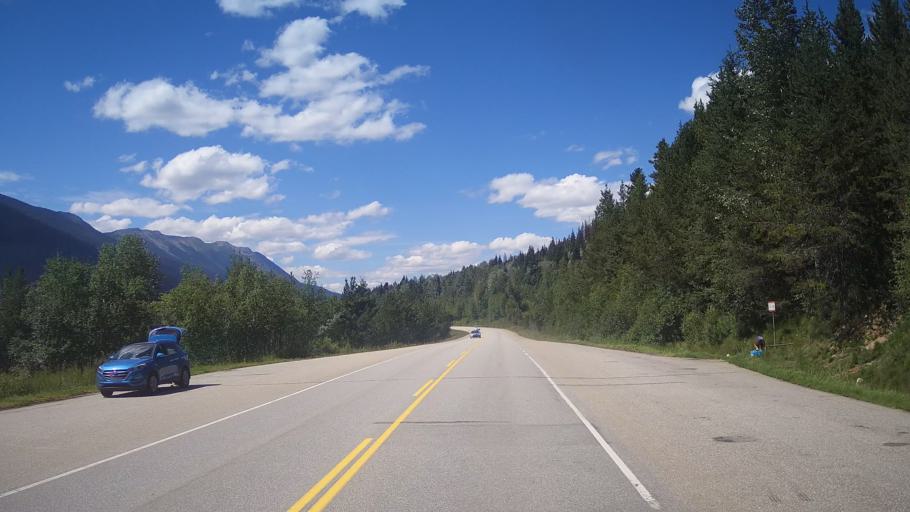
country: CA
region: Alberta
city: Jasper Park Lodge
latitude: 52.9705
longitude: -118.9351
